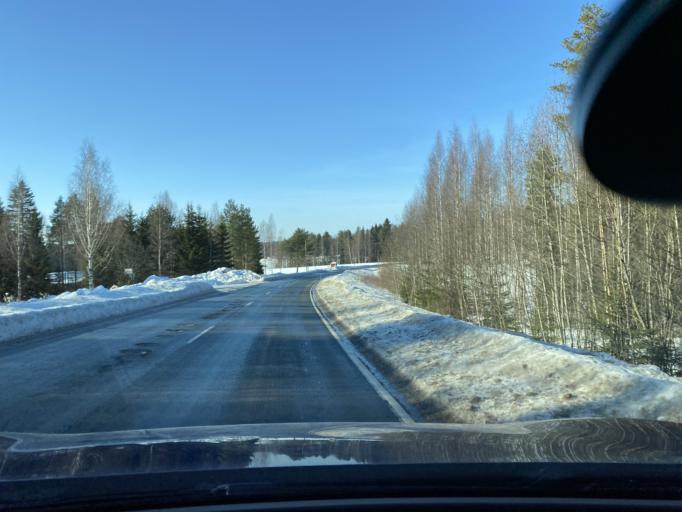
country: FI
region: Central Finland
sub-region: Joutsa
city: Joutsa
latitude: 61.7840
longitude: 26.0613
